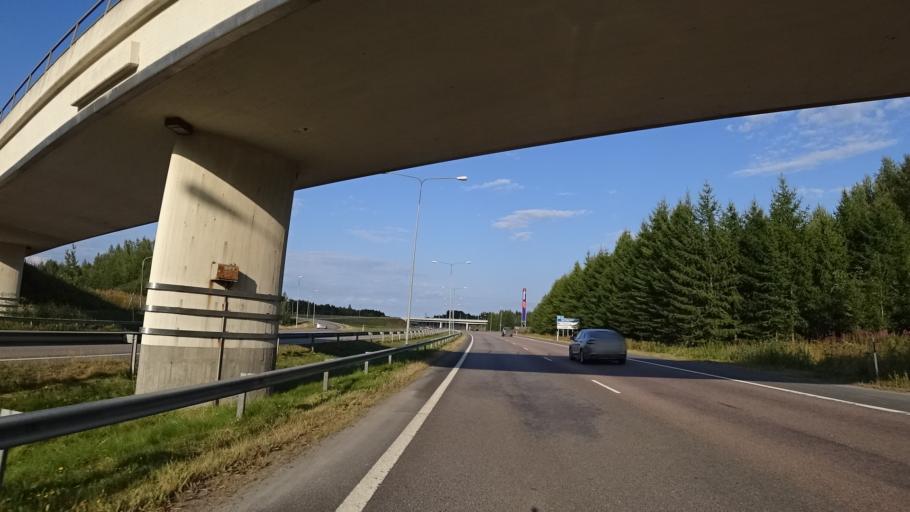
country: FI
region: South Karelia
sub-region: Imatra
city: Imatra
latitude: 61.2000
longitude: 28.8065
